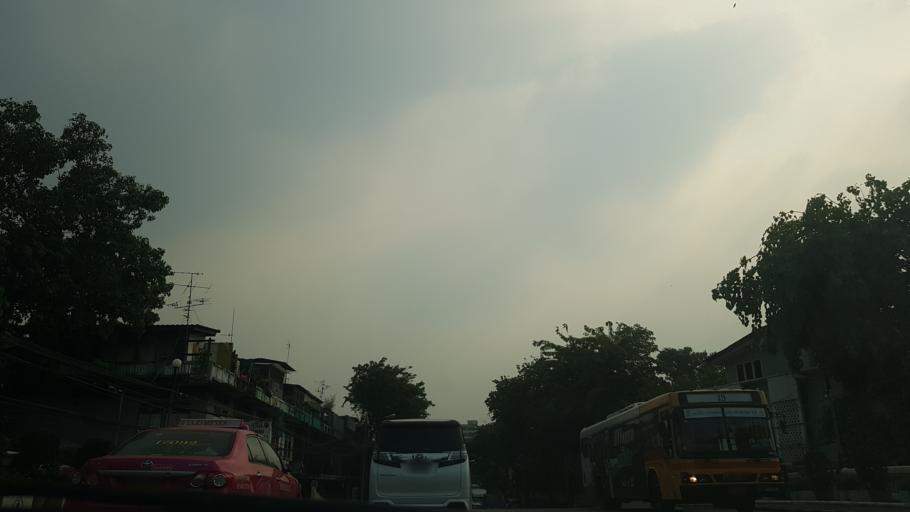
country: TH
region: Bangkok
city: Pom Prap Sattru Phai
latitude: 13.7549
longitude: 100.5095
